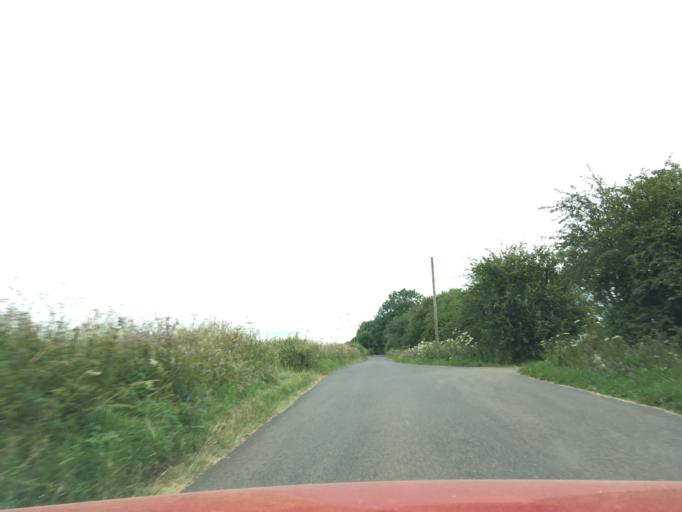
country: GB
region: England
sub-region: Gloucestershire
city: Shipton Village
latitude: 51.8935
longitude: -1.9144
